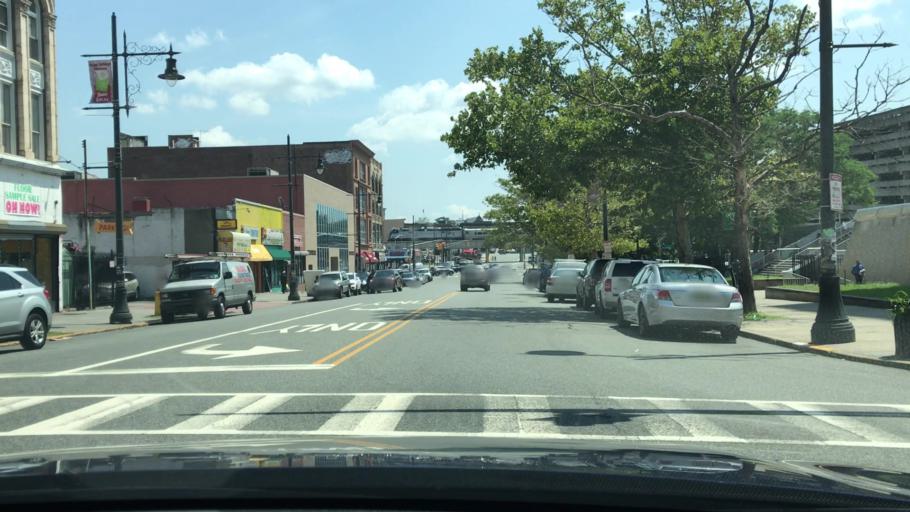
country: US
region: New Jersey
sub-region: Passaic County
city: Paterson
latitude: 40.9162
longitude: -74.1702
